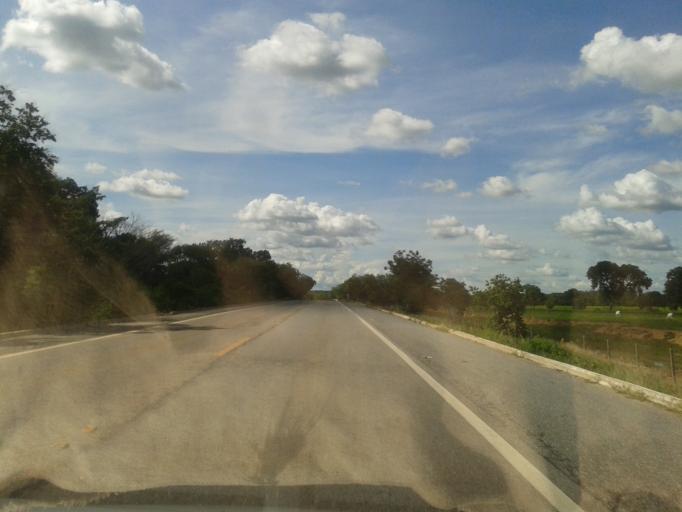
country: BR
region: Goias
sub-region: Mozarlandia
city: Mozarlandia
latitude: -15.1303
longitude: -50.5973
